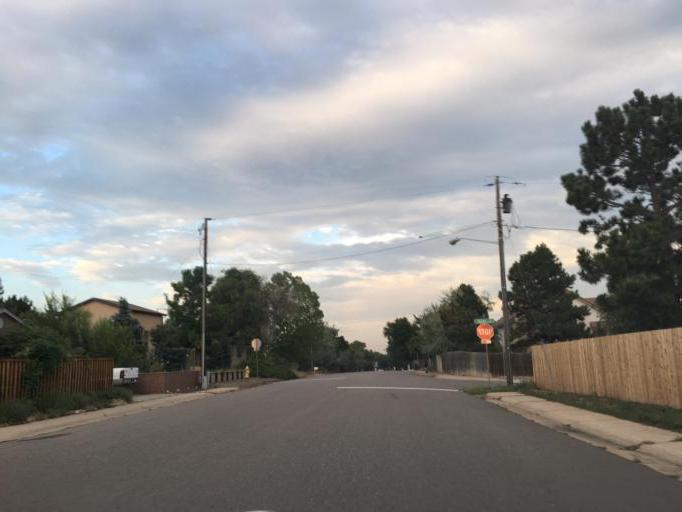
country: US
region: Colorado
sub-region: Adams County
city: Aurora
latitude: 39.6803
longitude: -104.8617
